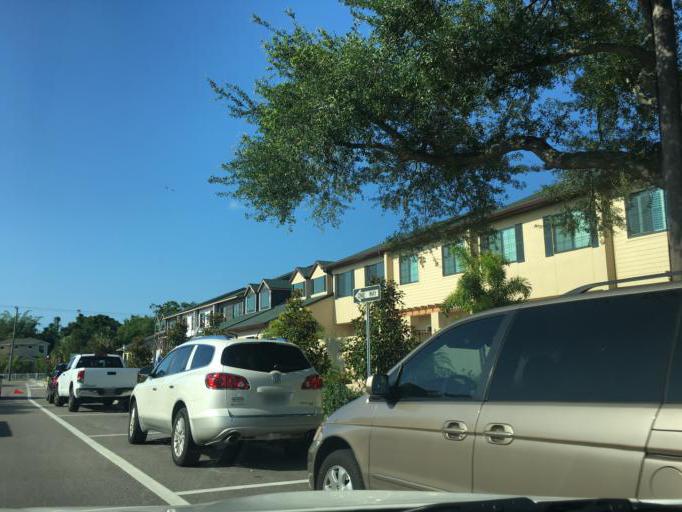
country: US
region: Florida
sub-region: Pinellas County
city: Saint Petersburg
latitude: 27.7802
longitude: -82.6457
